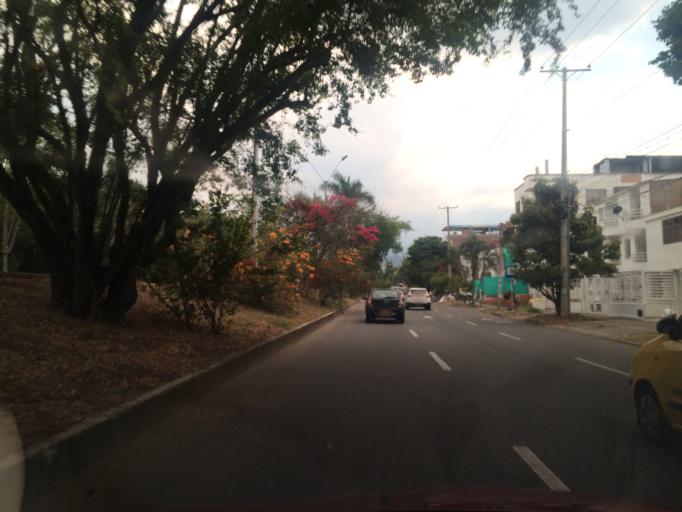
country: CO
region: Valle del Cauca
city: Cali
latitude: 3.3879
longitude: -76.5294
